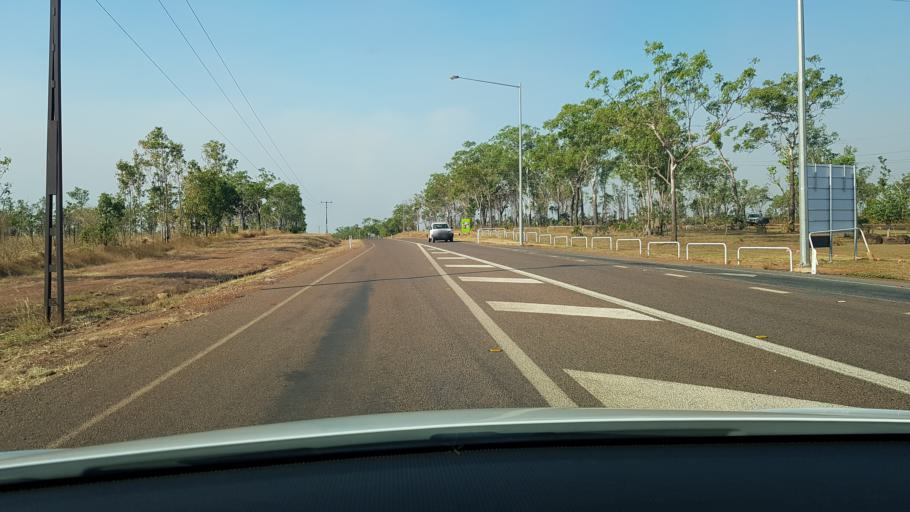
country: AU
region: Northern Territory
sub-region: Litchfield
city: McMinns Lagoon
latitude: -12.7002
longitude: 131.0156
